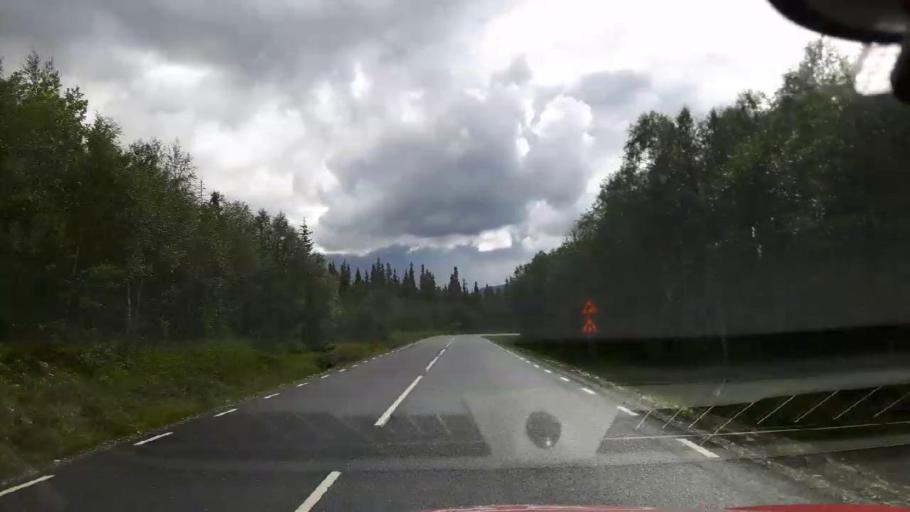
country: NO
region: Nord-Trondelag
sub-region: Royrvik
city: Royrvik
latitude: 64.8795
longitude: 14.2129
